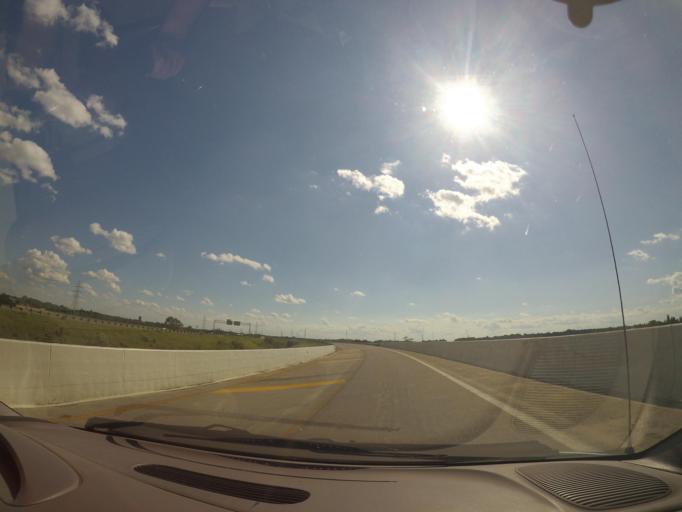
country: US
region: Ohio
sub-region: Sandusky County
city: Stony Prairie
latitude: 41.3684
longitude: -83.1582
